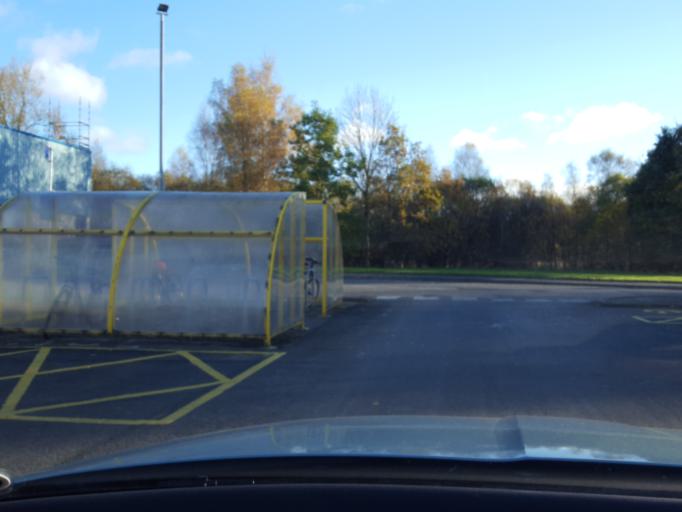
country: GB
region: Scotland
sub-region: East Dunbartonshire
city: Milngavie
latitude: 55.9314
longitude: -4.3115
